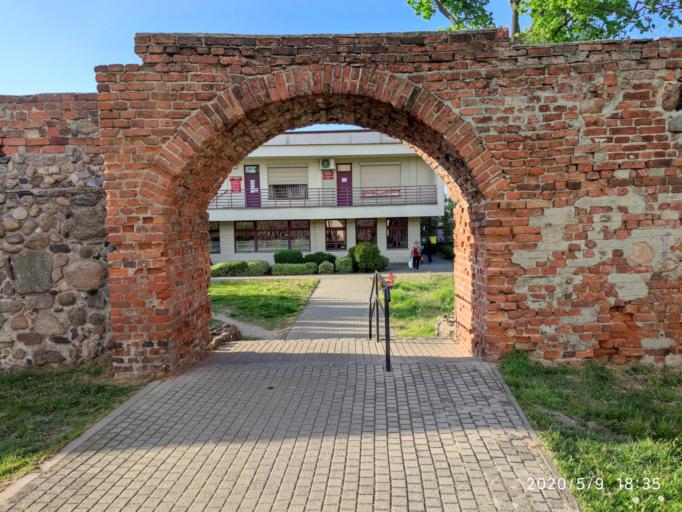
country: PL
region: Lubusz
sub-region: Powiat zielonogorski
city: Sulechow
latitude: 52.0869
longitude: 15.6269
